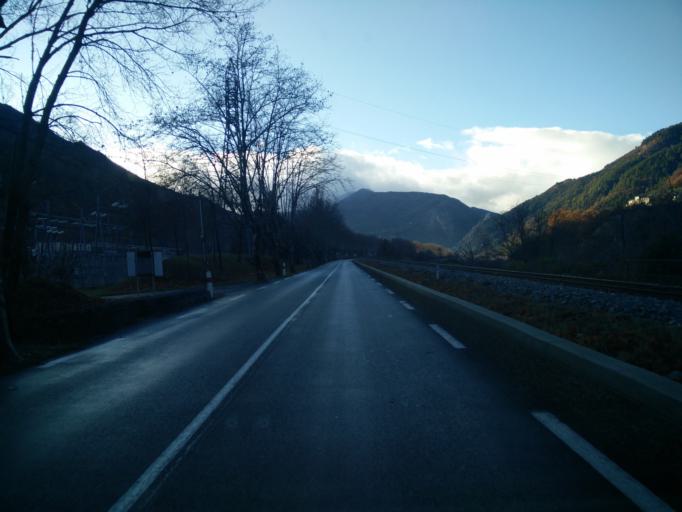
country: FR
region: Provence-Alpes-Cote d'Azur
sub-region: Departement des Alpes-Maritimes
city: Puget-Theniers
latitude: 43.9533
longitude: 6.8466
